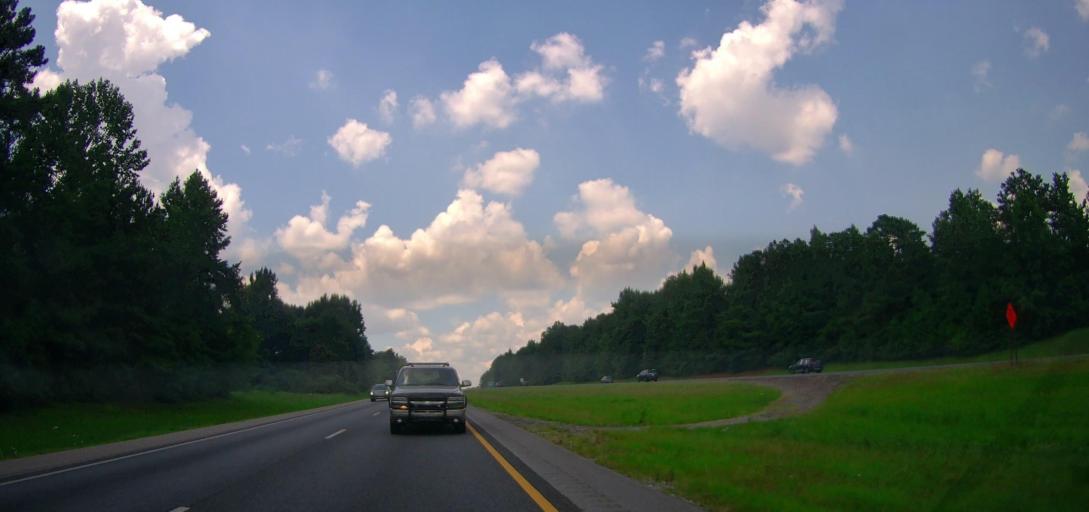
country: US
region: Alabama
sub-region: Chilton County
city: Clanton
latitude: 32.7888
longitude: -86.5756
